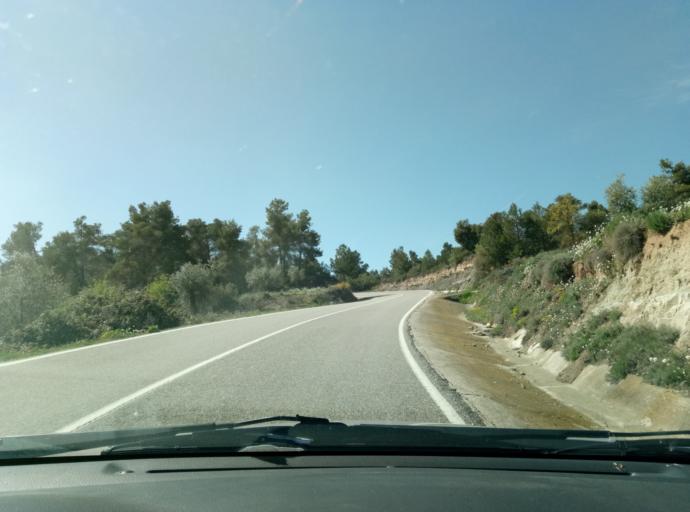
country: ES
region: Catalonia
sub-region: Provincia de Lleida
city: Vallbona de les Monges
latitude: 41.5336
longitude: 1.0246
